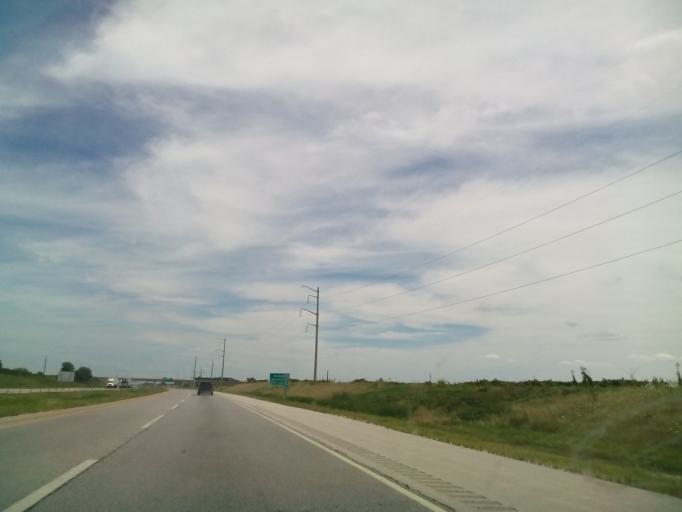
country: US
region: Illinois
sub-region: DeKalb County
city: DeKalb
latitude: 41.9005
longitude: -88.7303
